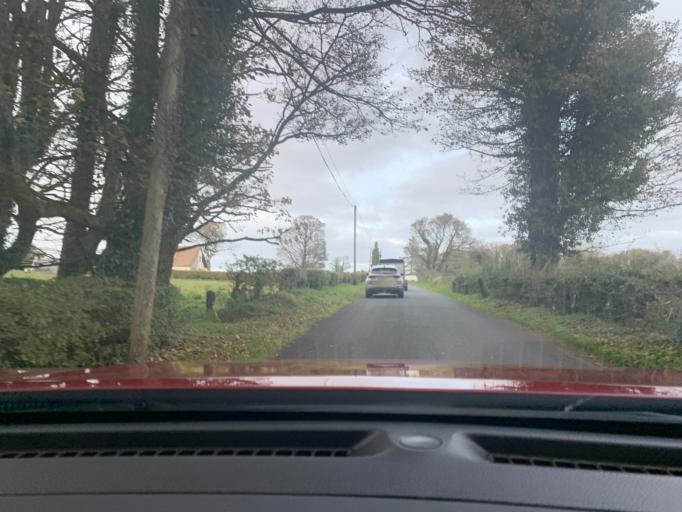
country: IE
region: Connaught
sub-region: Sligo
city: Tobercurry
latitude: 54.0370
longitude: -8.6924
